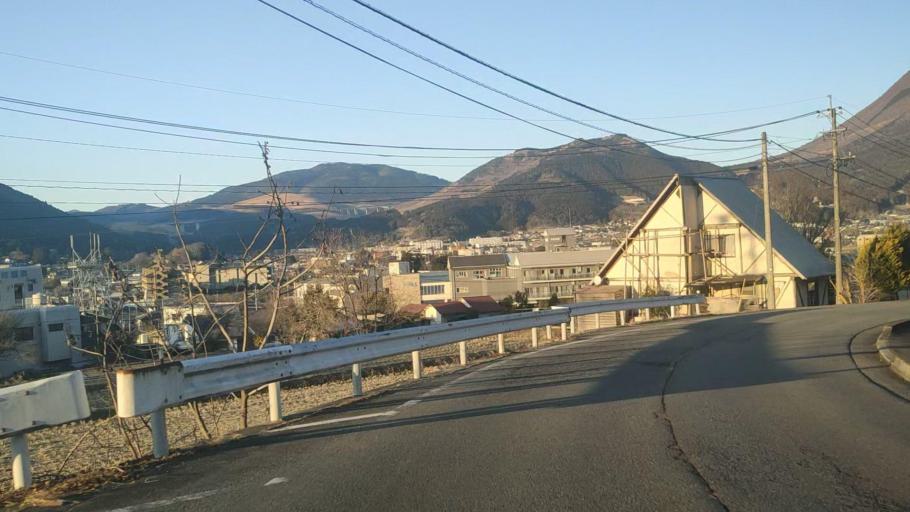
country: JP
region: Oita
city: Beppu
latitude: 33.2552
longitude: 131.3585
